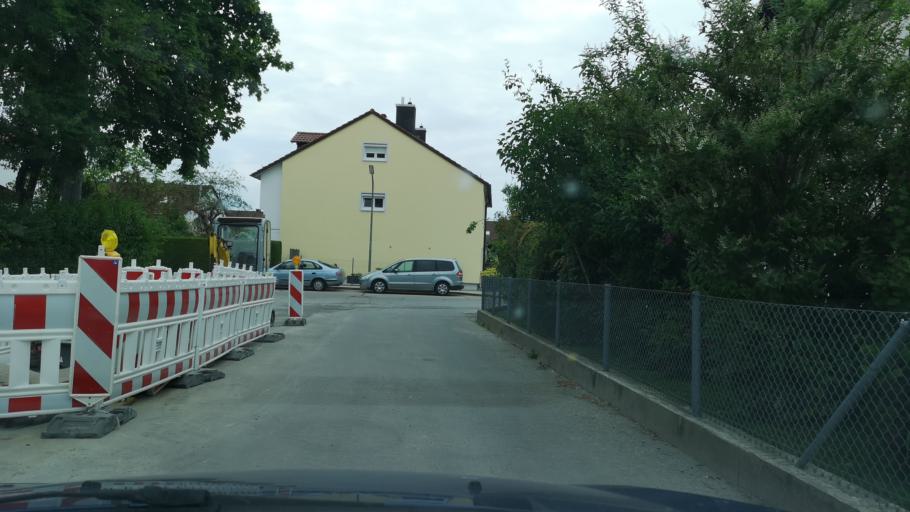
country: DE
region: Bavaria
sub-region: Upper Bavaria
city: Poing
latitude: 48.1671
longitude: 11.8109
